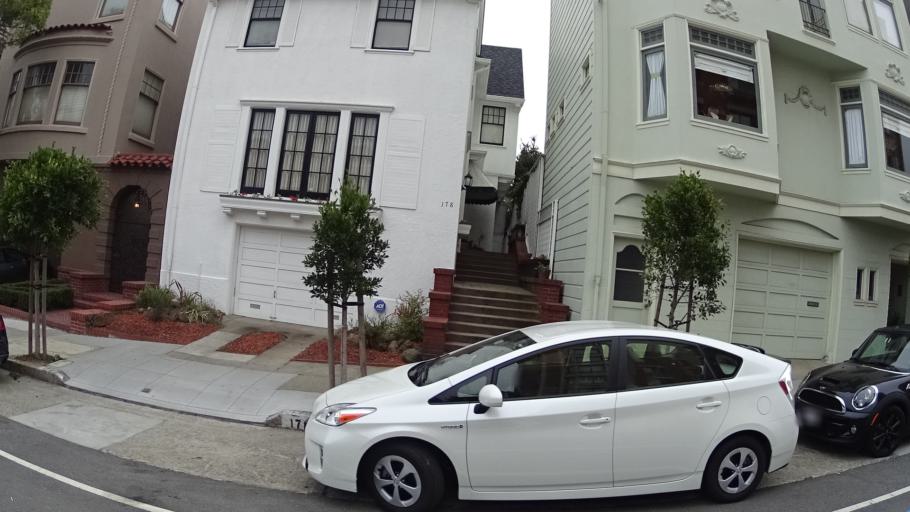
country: US
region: California
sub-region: San Francisco County
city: San Francisco
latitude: 37.7861
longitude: -122.4852
